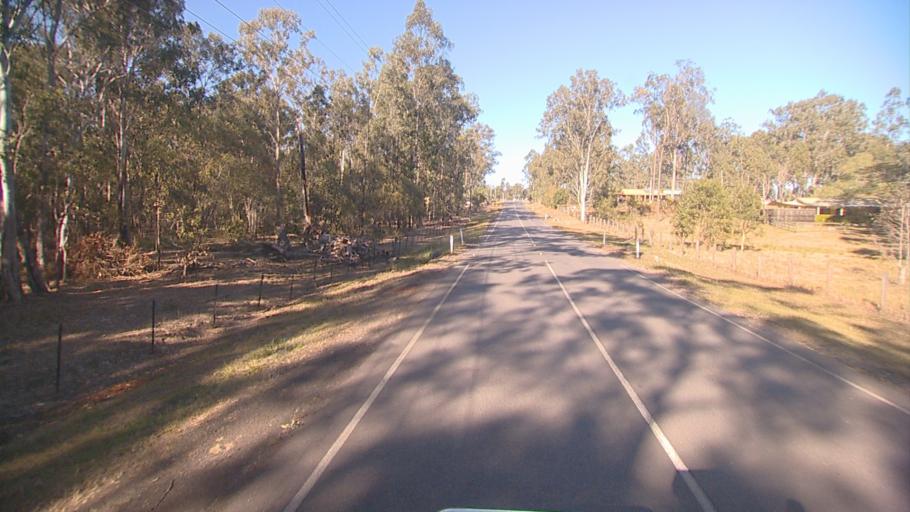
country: AU
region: Queensland
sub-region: Logan
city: North Maclean
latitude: -27.8194
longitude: 152.9879
